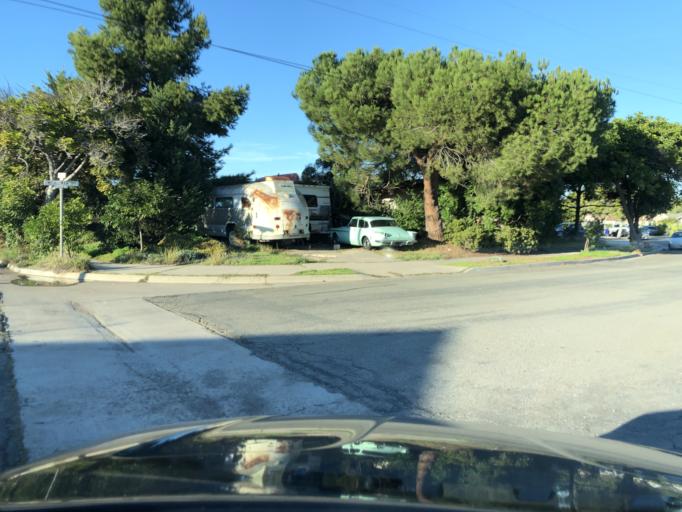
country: US
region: California
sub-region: San Diego County
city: La Jolla
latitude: 32.8151
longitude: -117.1956
